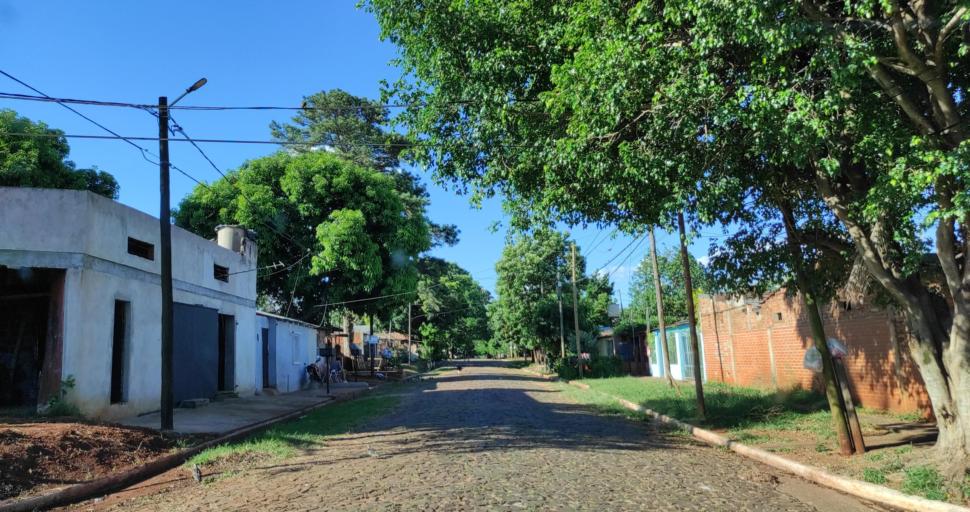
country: AR
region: Misiones
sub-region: Departamento de Capital
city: Posadas
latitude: -27.3800
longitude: -55.9240
